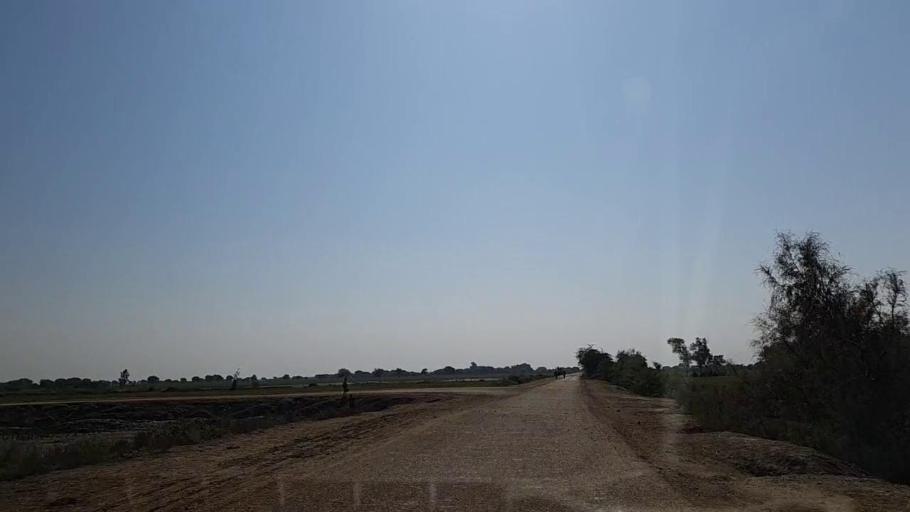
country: PK
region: Sindh
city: Chuhar Jamali
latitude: 24.5212
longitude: 68.0933
